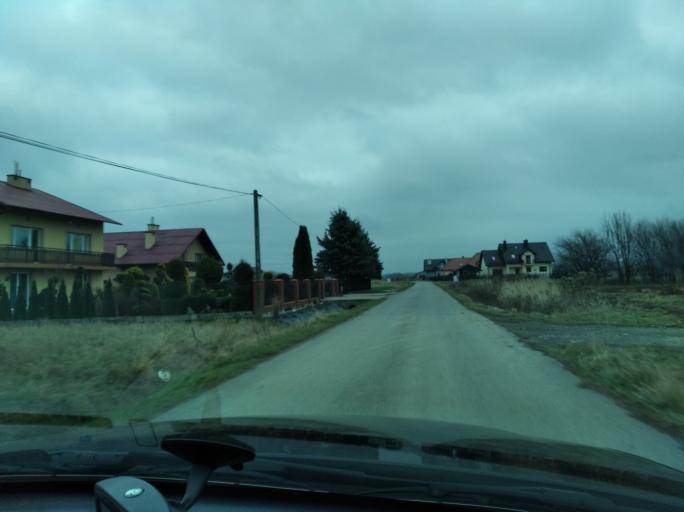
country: PL
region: Subcarpathian Voivodeship
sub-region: Powiat rzeszowski
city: Lutoryz
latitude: 49.9653
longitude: 21.9305
